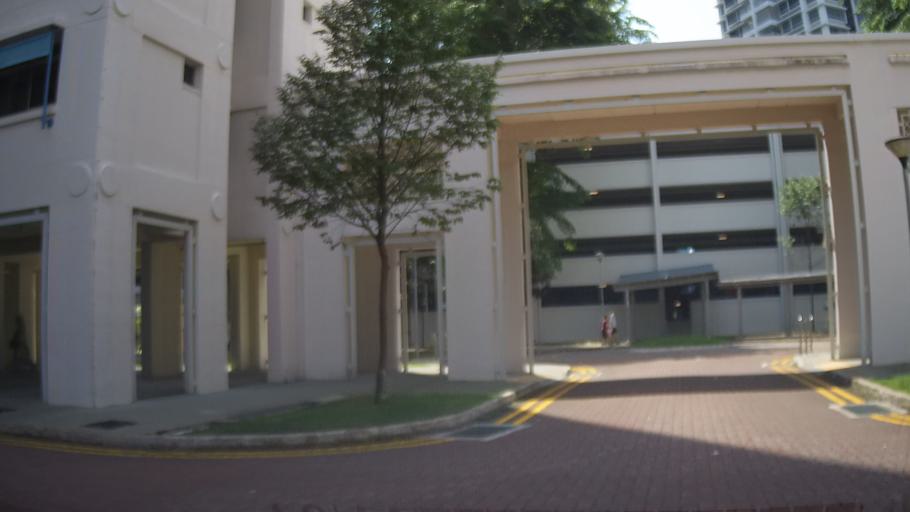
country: SG
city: Singapore
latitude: 1.3169
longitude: 103.8608
